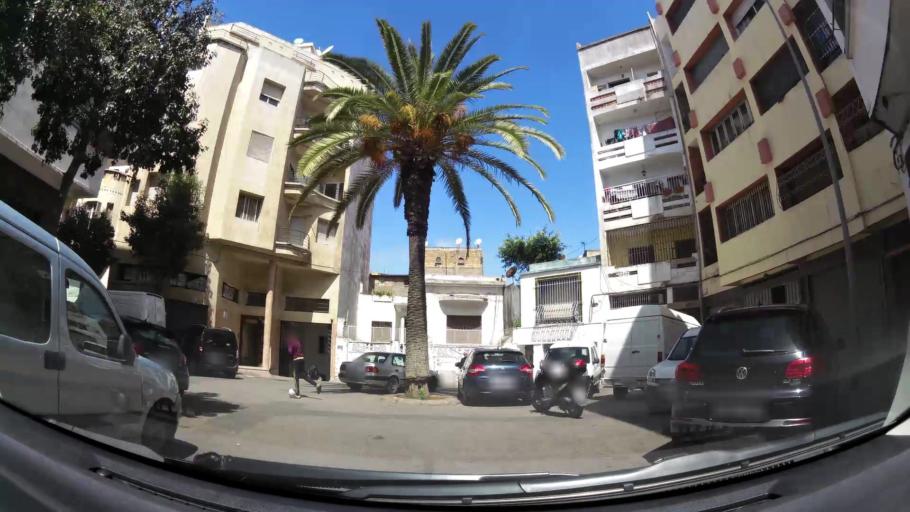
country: MA
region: Grand Casablanca
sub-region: Casablanca
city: Casablanca
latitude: 33.5969
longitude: -7.6256
